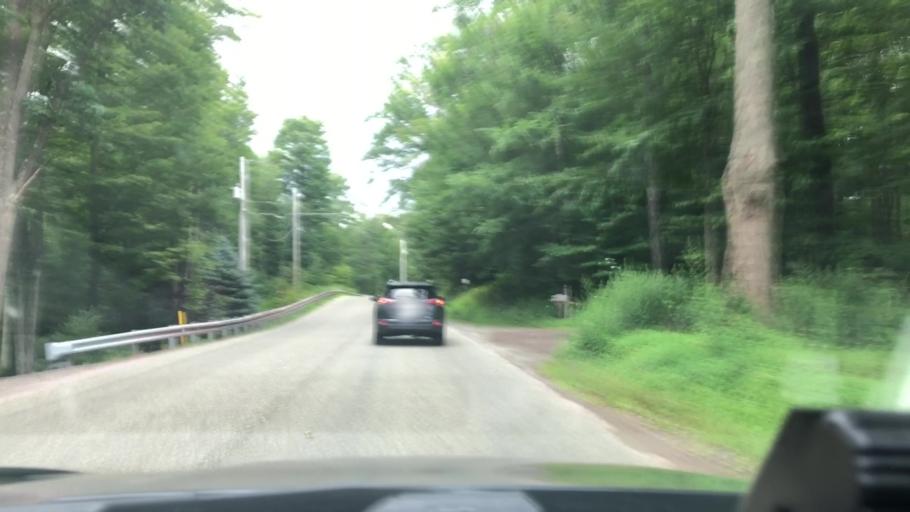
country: US
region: Pennsylvania
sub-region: Lackawanna County
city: Moscow
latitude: 41.2356
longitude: -75.4889
